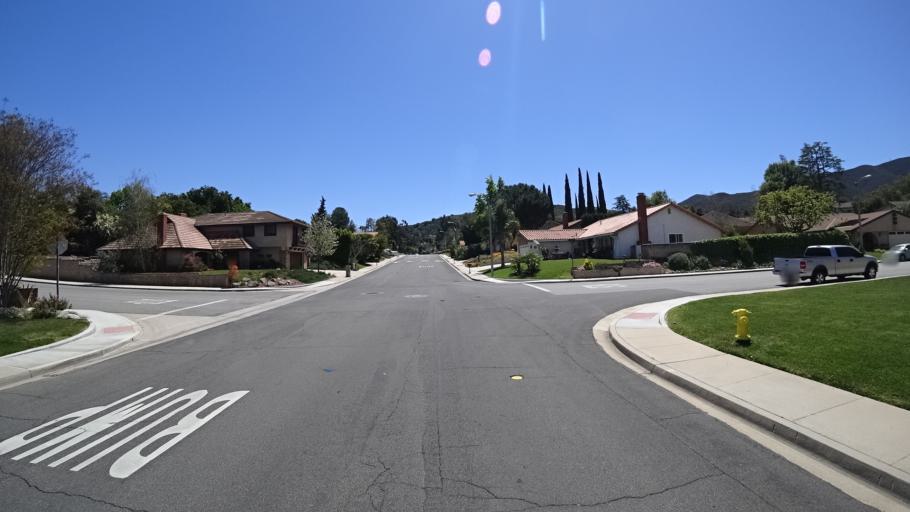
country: US
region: California
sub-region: Ventura County
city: Casa Conejo
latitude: 34.1794
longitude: -118.8955
